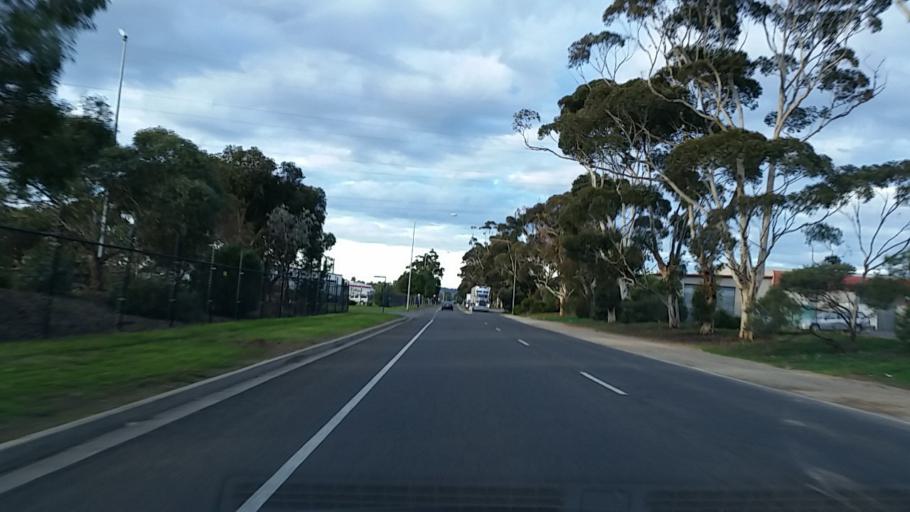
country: AU
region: South Australia
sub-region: Port Adelaide Enfield
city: Enfield
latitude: -34.8290
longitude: 138.6079
